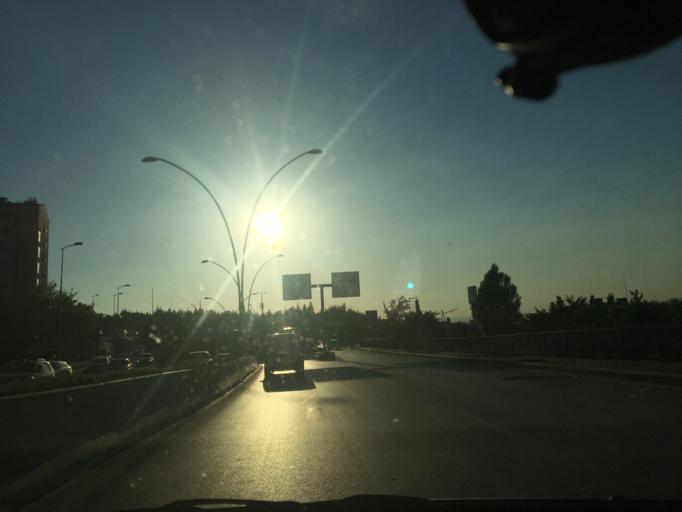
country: TR
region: Ankara
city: Ankara
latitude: 39.8967
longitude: 32.8444
